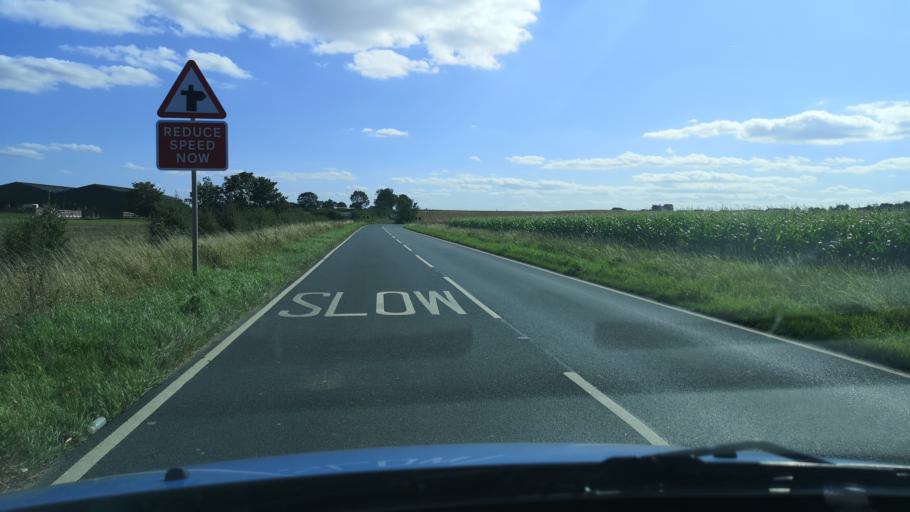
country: GB
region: England
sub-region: North Lincolnshire
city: Crowle
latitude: 53.6162
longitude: -0.8189
